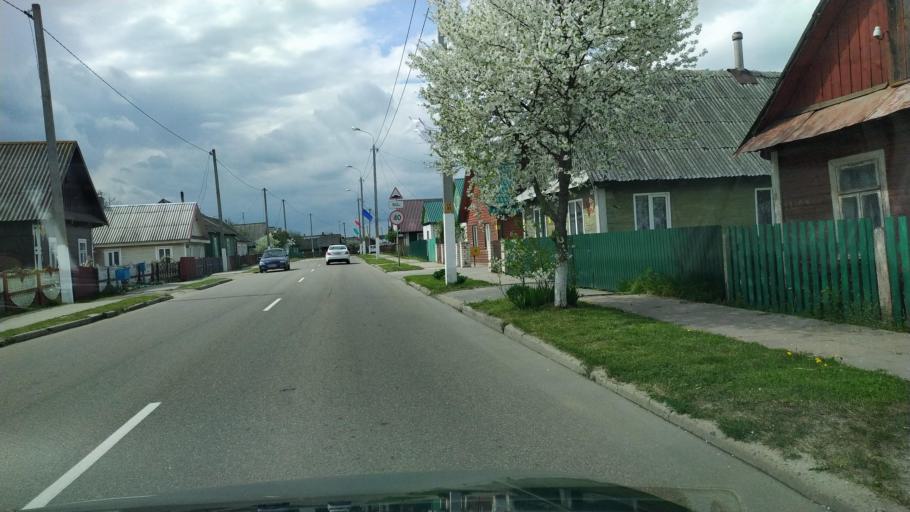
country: BY
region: Brest
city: Pruzhany
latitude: 52.5560
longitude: 24.4403
